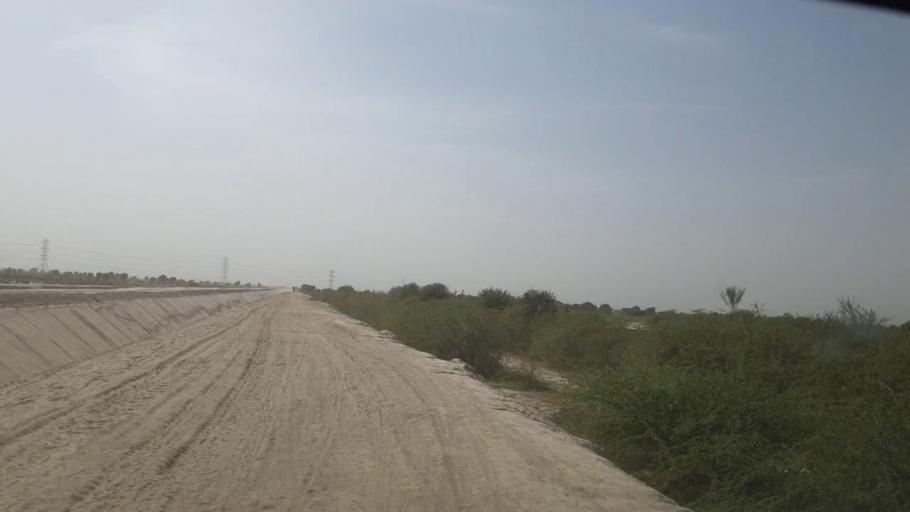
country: PK
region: Sindh
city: Nabisar
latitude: 25.0582
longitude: 69.5567
